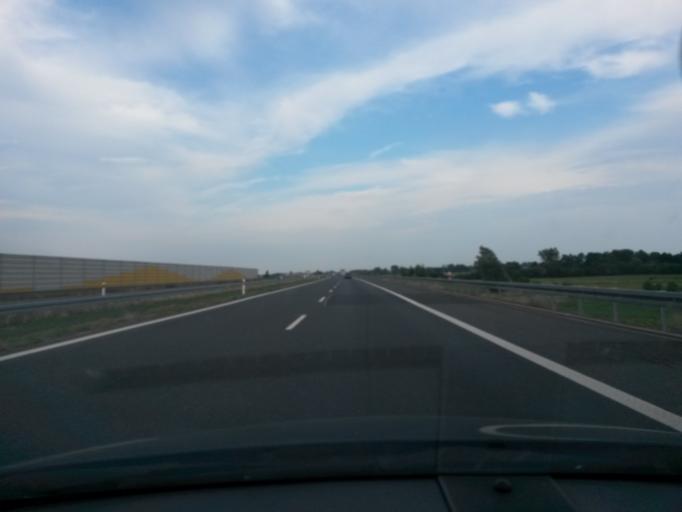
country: PL
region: Lodz Voivodeship
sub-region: Powiat poddebicki
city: Wartkowice
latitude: 52.0009
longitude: 19.0003
